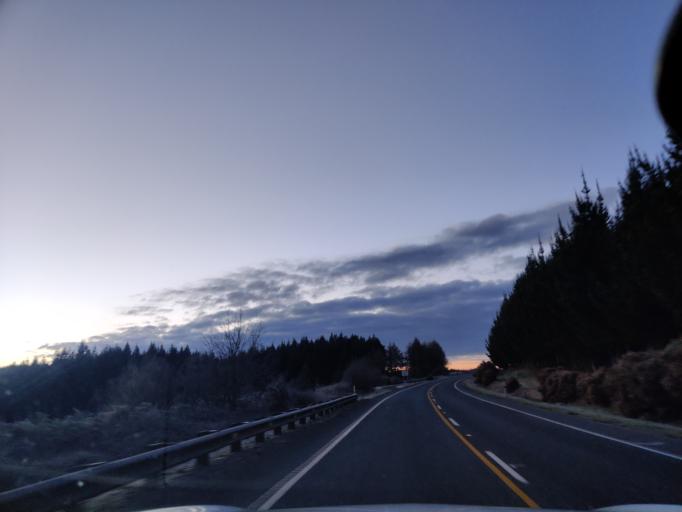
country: NZ
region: Waikato
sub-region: South Waikato District
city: Tokoroa
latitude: -38.3288
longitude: 175.9971
